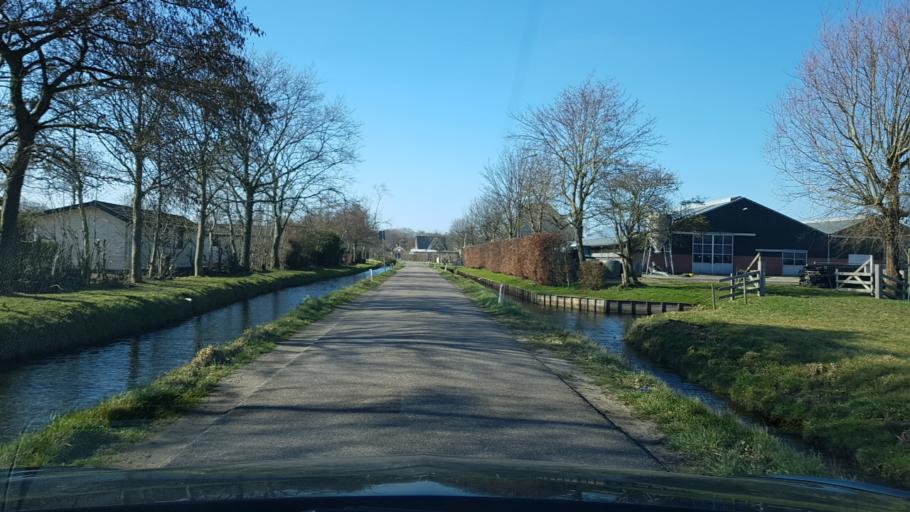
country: NL
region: North Holland
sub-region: Gemeente Heiloo
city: Heiloo
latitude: 52.6341
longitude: 4.6644
